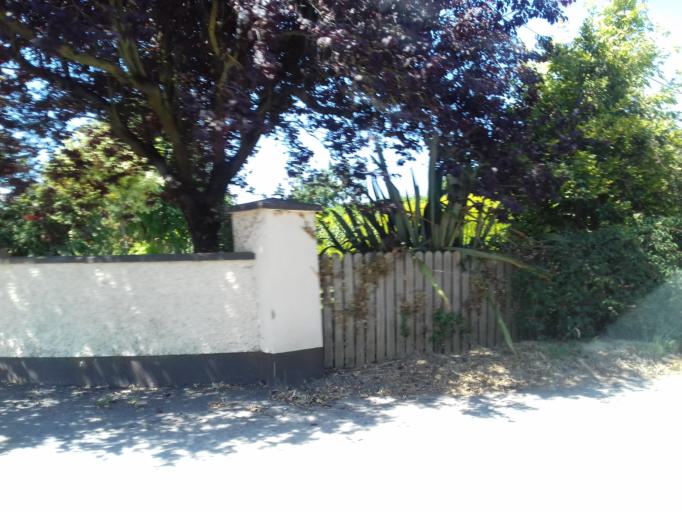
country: IE
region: Leinster
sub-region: An Mhi
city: Ashbourne
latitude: 53.5275
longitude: -6.3022
